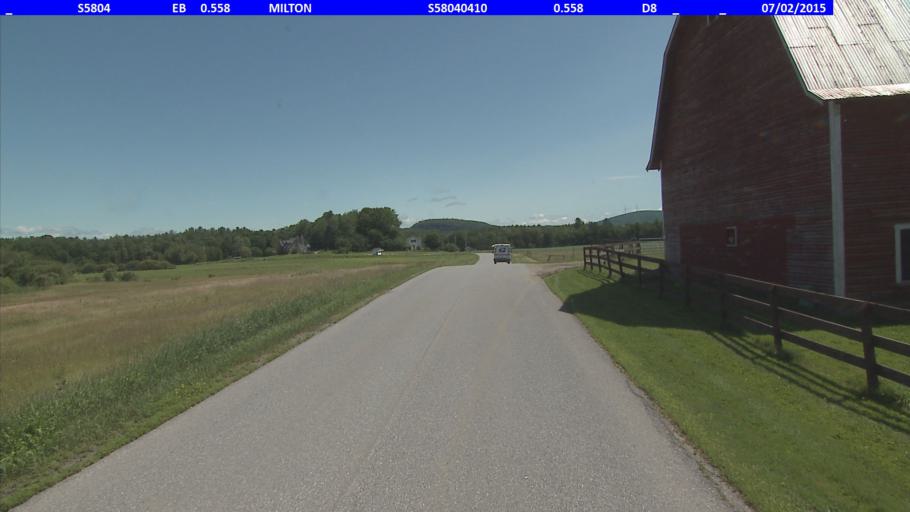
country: US
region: Vermont
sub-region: Chittenden County
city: Milton
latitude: 44.6541
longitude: -73.1614
